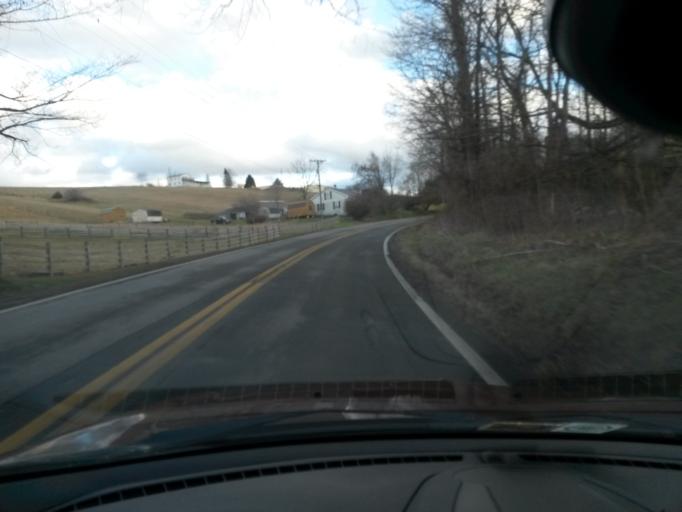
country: US
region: West Virginia
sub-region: Monroe County
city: Union
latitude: 37.5876
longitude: -80.5070
